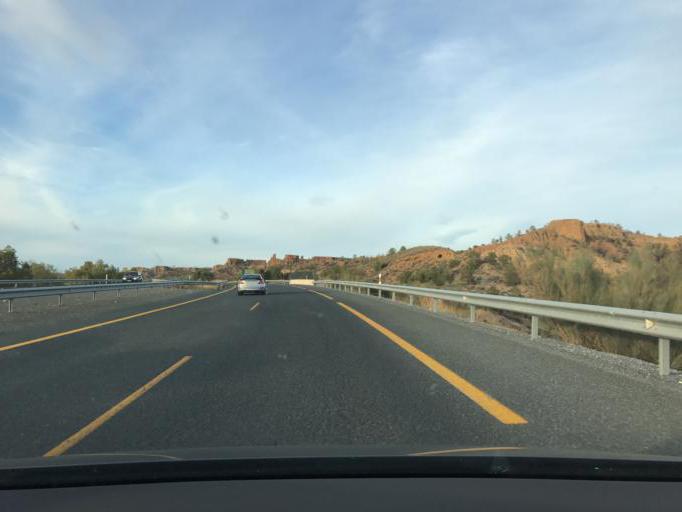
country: ES
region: Andalusia
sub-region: Provincia de Granada
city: Guadix
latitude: 37.2980
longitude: -3.1097
